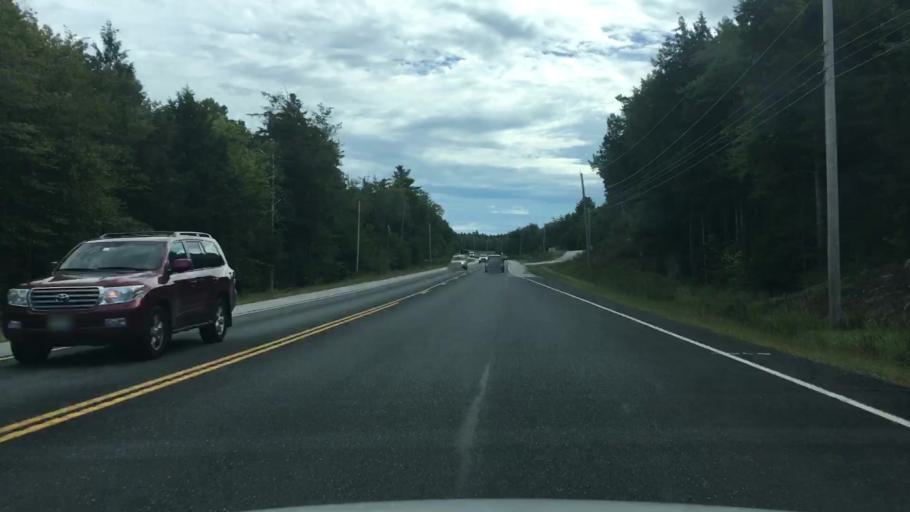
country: US
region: Maine
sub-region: Hancock County
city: Dedham
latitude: 44.6633
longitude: -68.5664
